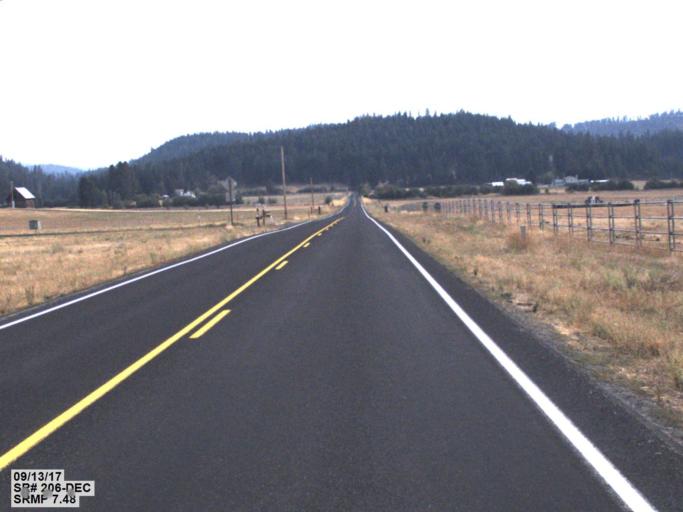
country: US
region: Washington
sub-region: Spokane County
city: Trentwood
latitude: 47.8107
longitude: -117.2129
